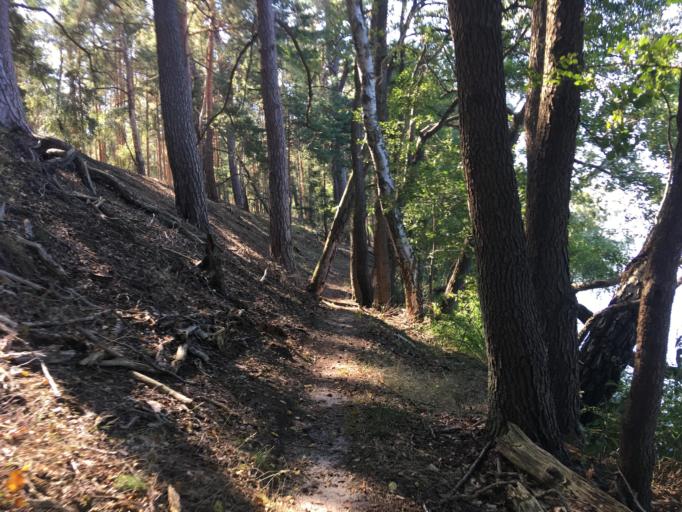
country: DE
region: Brandenburg
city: Gross Koris
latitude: 52.2099
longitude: 13.7512
